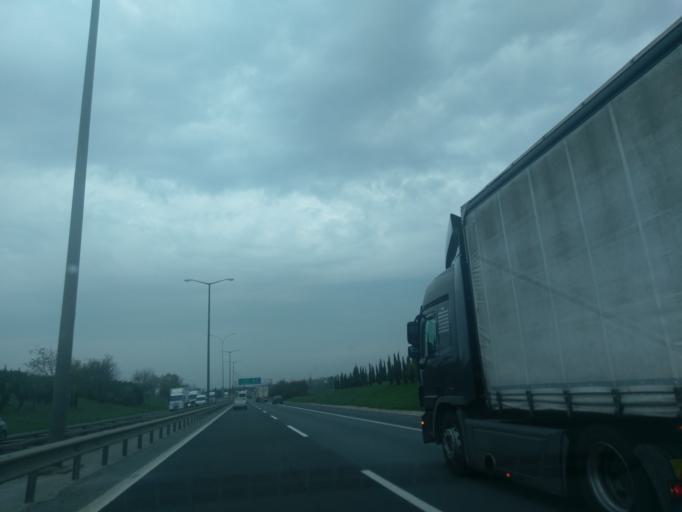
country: TR
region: Istanbul
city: Muratbey
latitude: 41.0800
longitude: 28.5080
